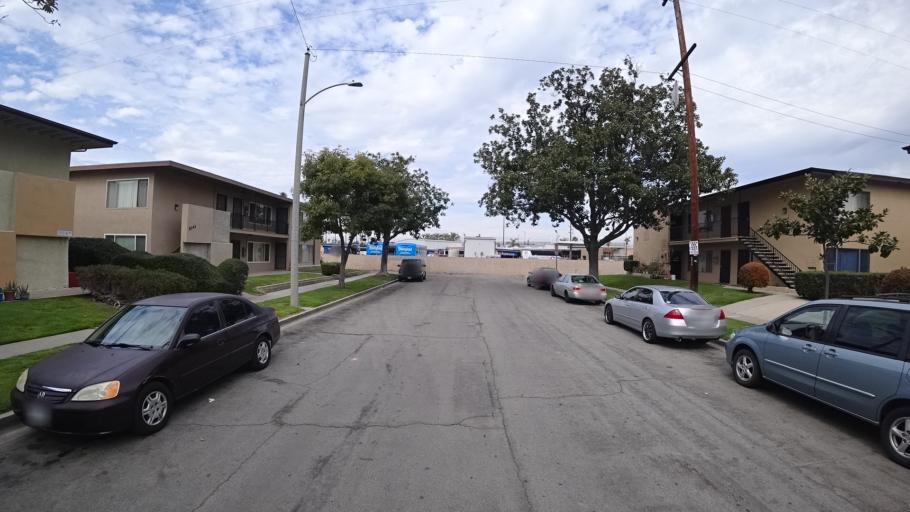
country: US
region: California
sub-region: Orange County
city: Anaheim
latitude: 33.7976
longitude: -117.8994
